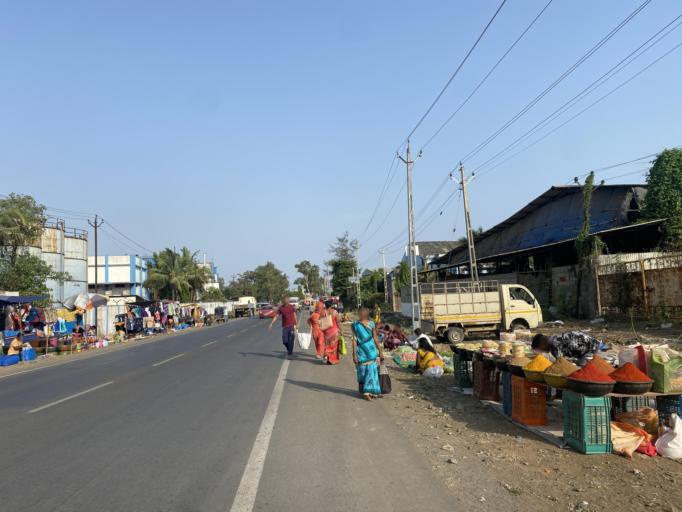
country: IN
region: Gujarat
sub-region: Valsad
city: Vapi
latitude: 20.3033
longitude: 72.8486
